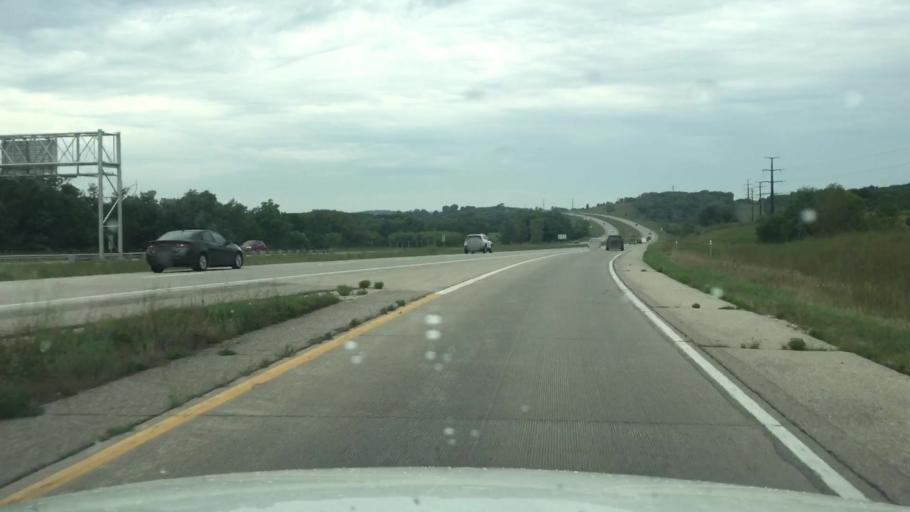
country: US
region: Iowa
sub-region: Warren County
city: Carlisle
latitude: 41.5053
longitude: -93.5791
